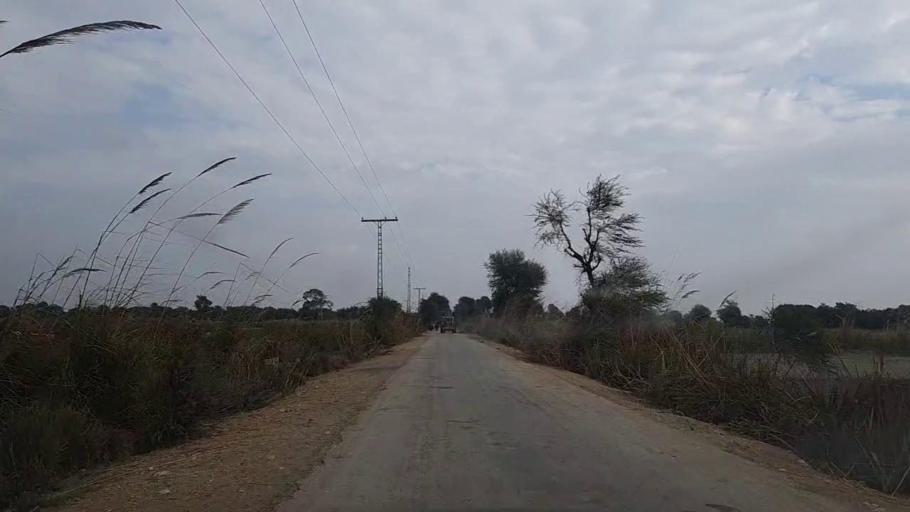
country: PK
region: Sindh
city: Sanghar
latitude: 26.2301
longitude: 68.9944
